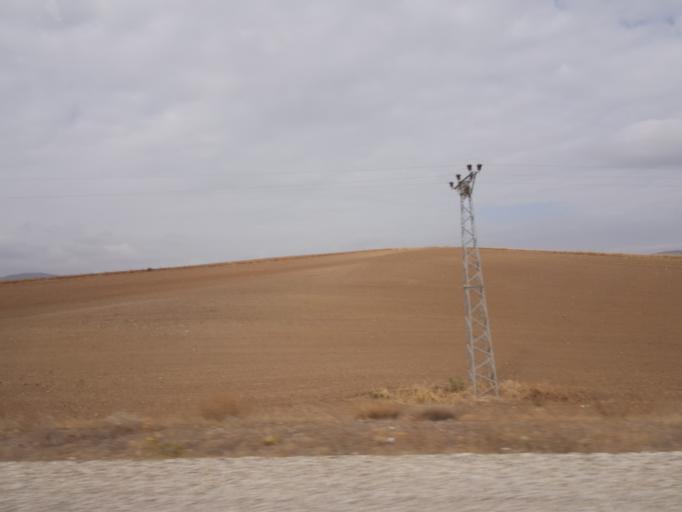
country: TR
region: Kirikkale
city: Bahsili
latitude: 39.6967
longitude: 33.4174
